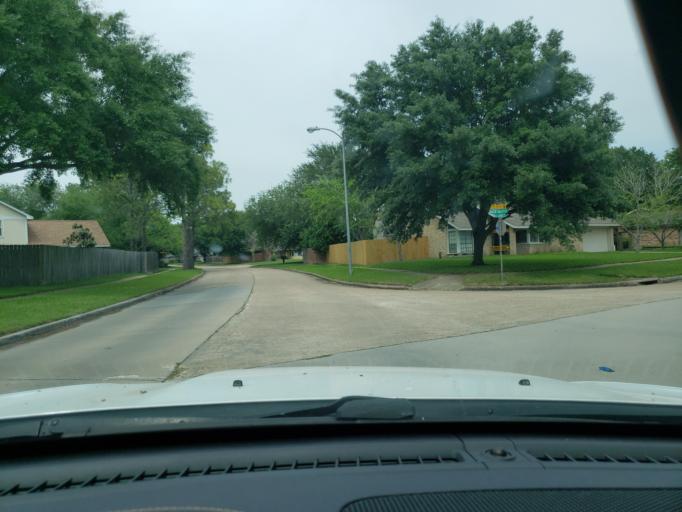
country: US
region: Texas
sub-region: Harris County
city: Jersey Village
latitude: 29.9140
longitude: -95.5732
